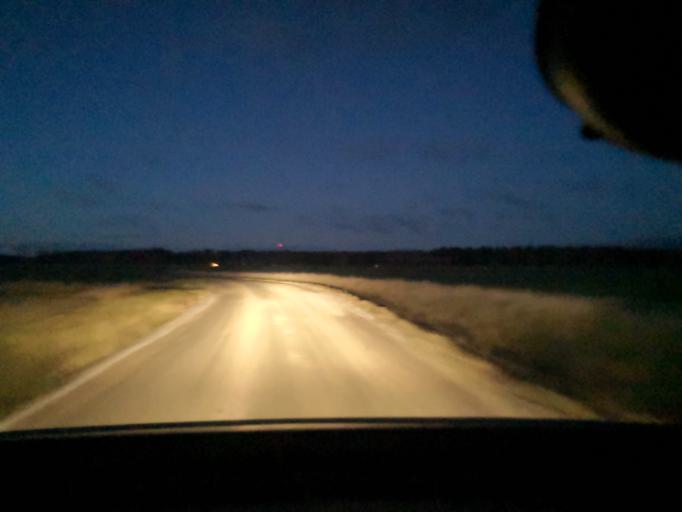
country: SE
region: Uppsala
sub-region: Heby Kommun
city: Heby
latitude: 59.9247
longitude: 16.7547
